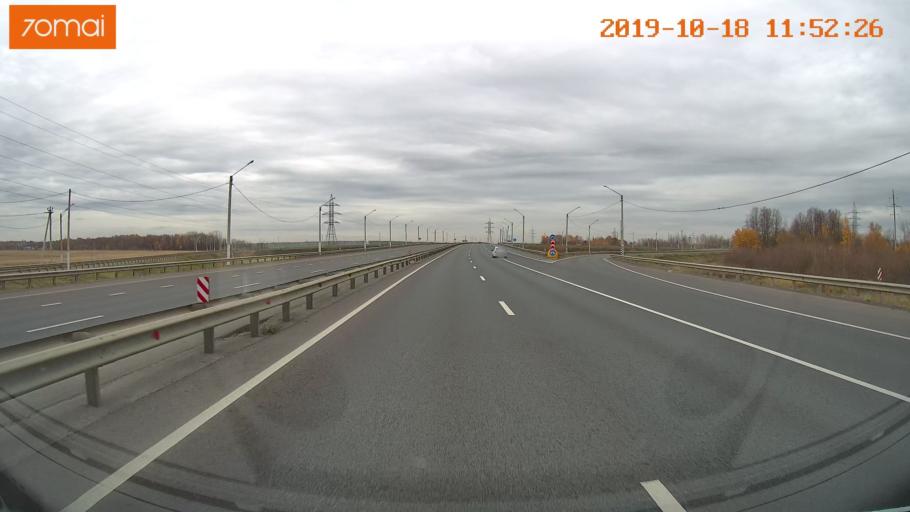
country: RU
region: Rjazan
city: Mikhaylov
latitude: 54.2483
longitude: 39.0486
